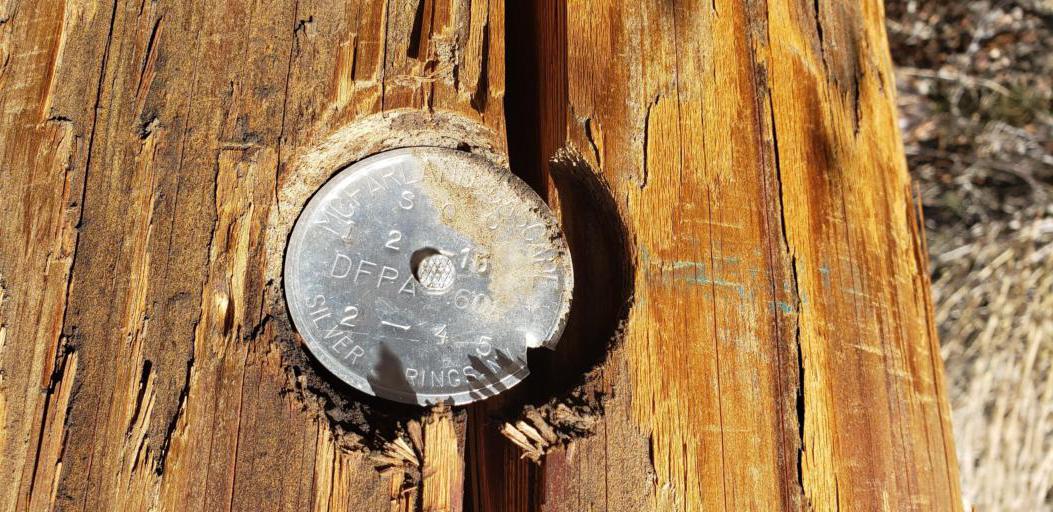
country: US
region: California
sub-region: San Bernardino County
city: Big Bear City
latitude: 34.3045
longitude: -116.8312
